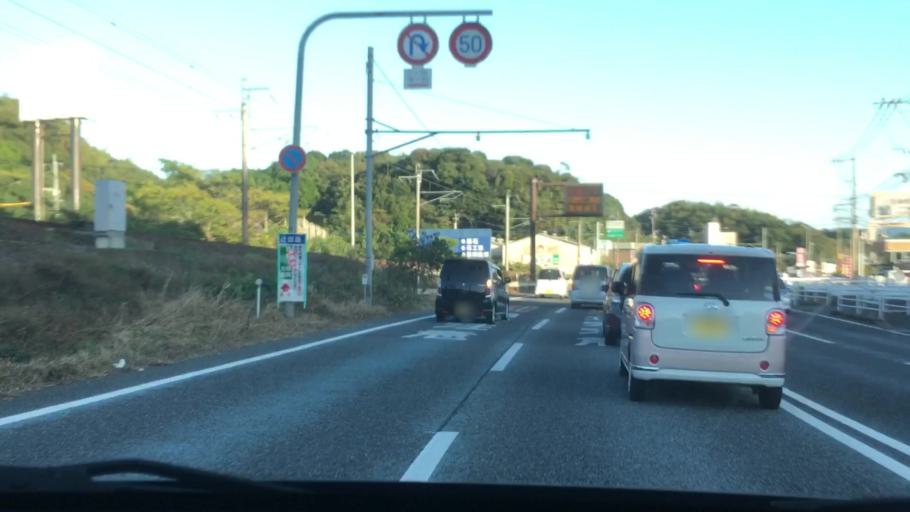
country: JP
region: Nagasaki
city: Sasebo
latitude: 33.1524
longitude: 129.7783
